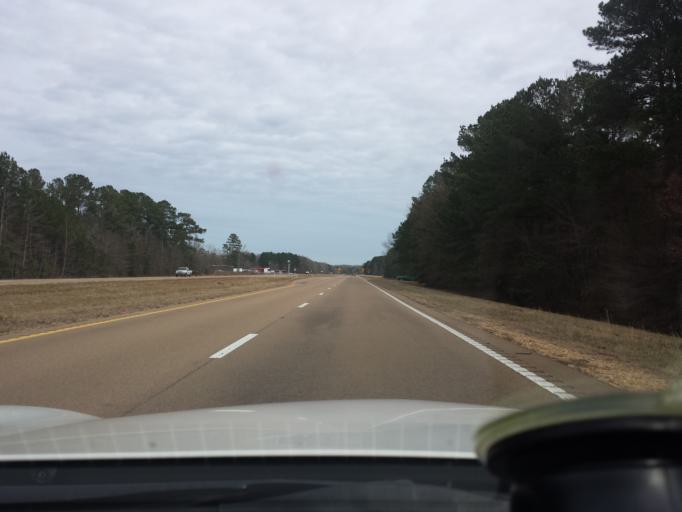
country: US
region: Mississippi
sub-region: Scott County
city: Morton
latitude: 32.5674
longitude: -89.7437
